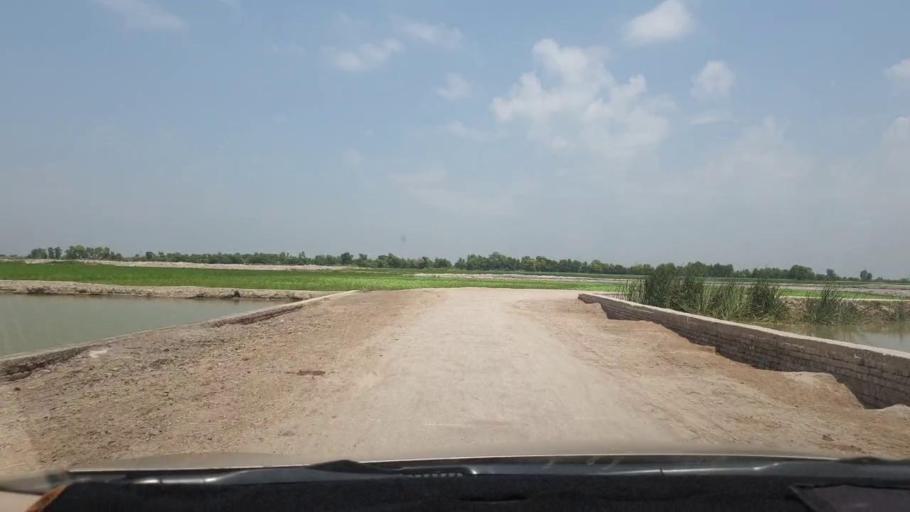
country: PK
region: Sindh
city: Naudero
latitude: 27.7343
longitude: 68.3296
